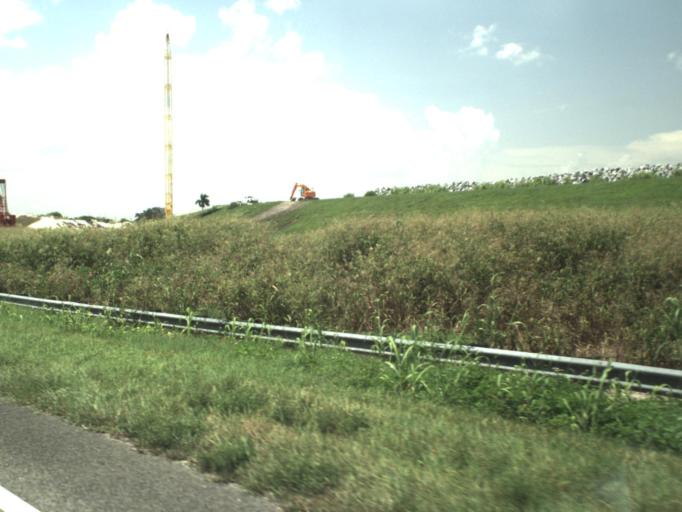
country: US
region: Florida
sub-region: Palm Beach County
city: South Bay
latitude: 26.6813
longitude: -80.7478
